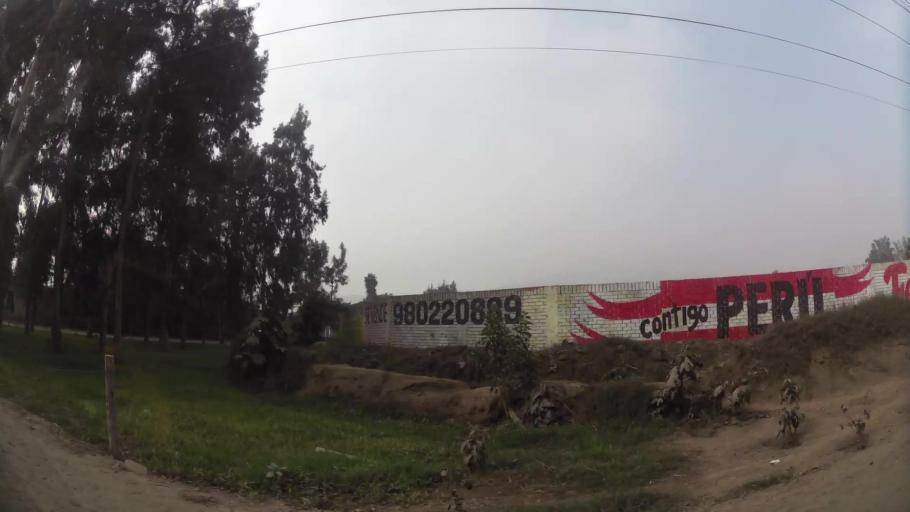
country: PE
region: Lima
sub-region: Lima
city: Santa Maria
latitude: -12.0069
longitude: -76.8350
